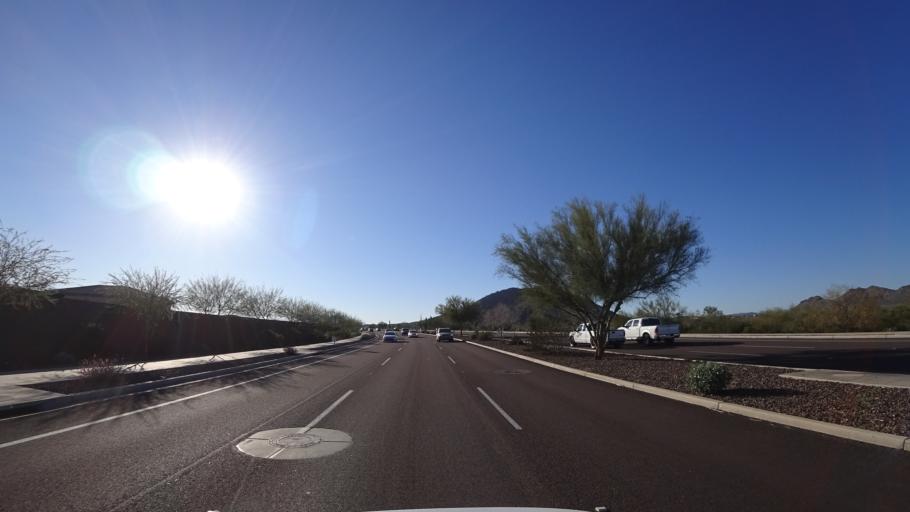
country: US
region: Arizona
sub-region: Maricopa County
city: Sun City
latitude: 33.7107
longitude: -112.2275
